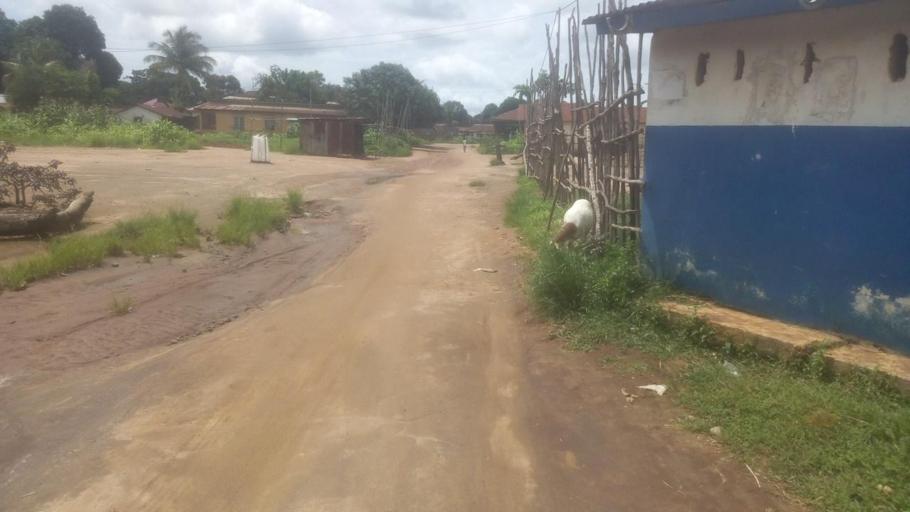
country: SL
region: Northern Province
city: Masoyila
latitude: 8.6050
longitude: -13.1855
